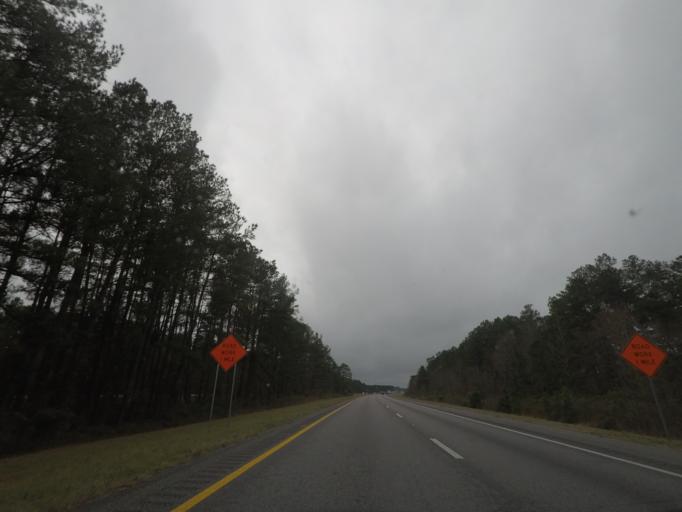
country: US
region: South Carolina
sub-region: Orangeburg County
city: Holly Hill
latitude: 33.3288
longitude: -80.5412
